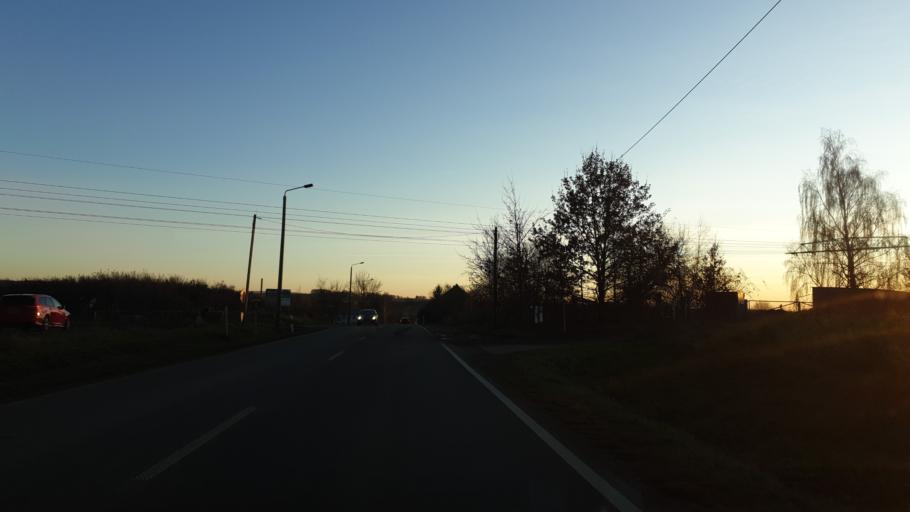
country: DE
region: Saxony
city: Kirchberg
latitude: 50.7992
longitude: 12.7564
